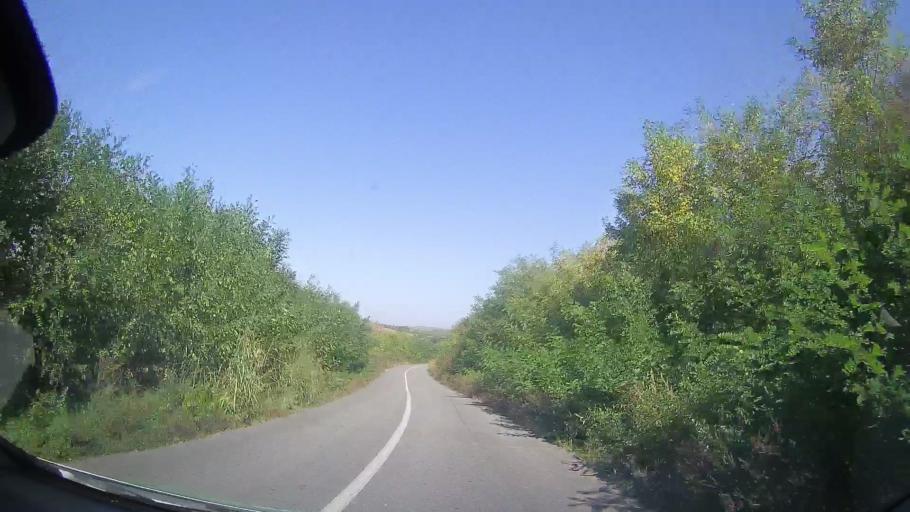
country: RO
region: Timis
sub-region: Comuna Balint
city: Balint
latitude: 45.8351
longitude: 21.8563
